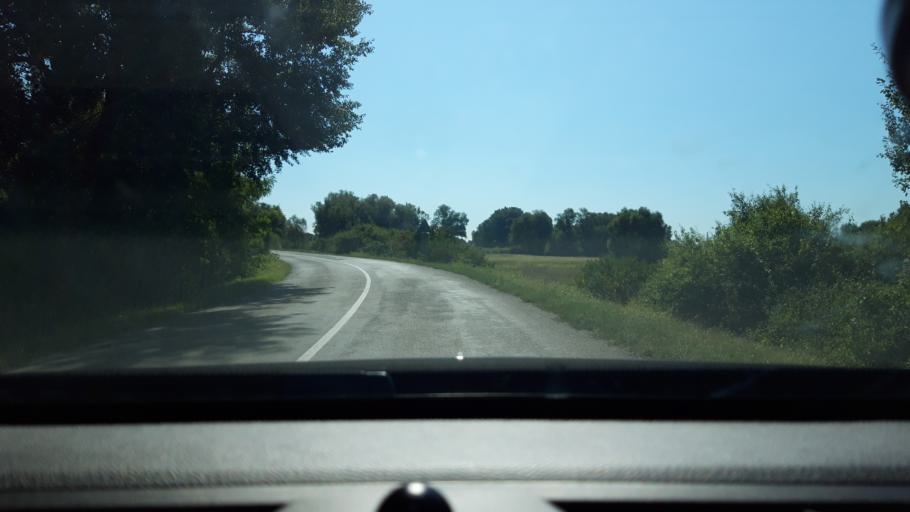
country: SK
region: Kosicky
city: Michalovce
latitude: 48.6054
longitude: 21.9518
